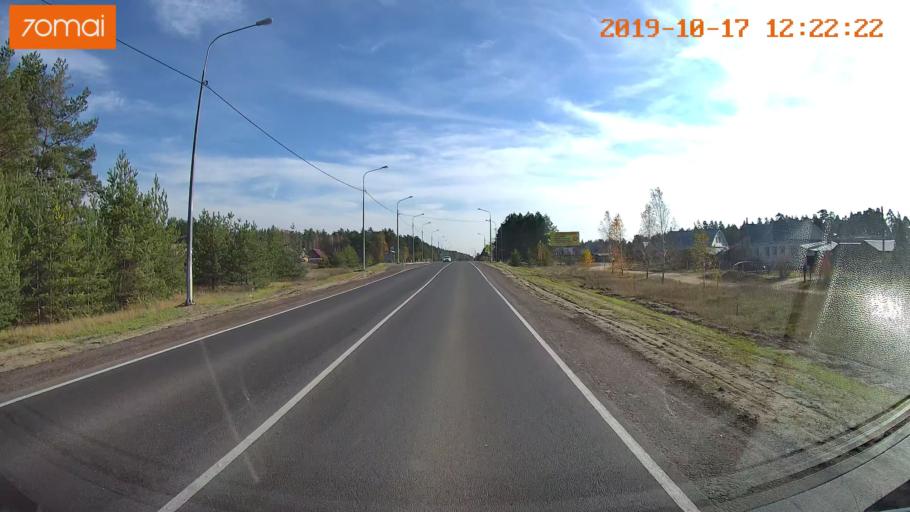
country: RU
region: Rjazan
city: Gus'-Zheleznyy
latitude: 55.0525
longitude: 41.1706
